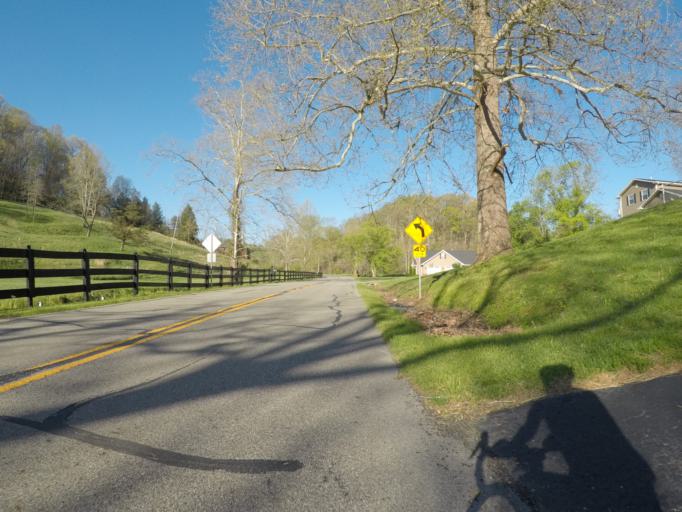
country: US
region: Kentucky
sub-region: Boyd County
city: Meads
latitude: 38.3659
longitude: -82.6661
